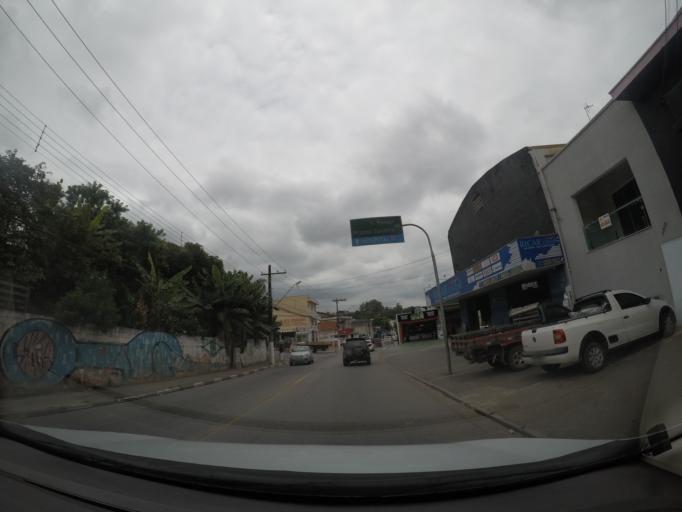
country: BR
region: Sao Paulo
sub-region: Aruja
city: Aruja
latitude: -23.3933
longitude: -46.3197
